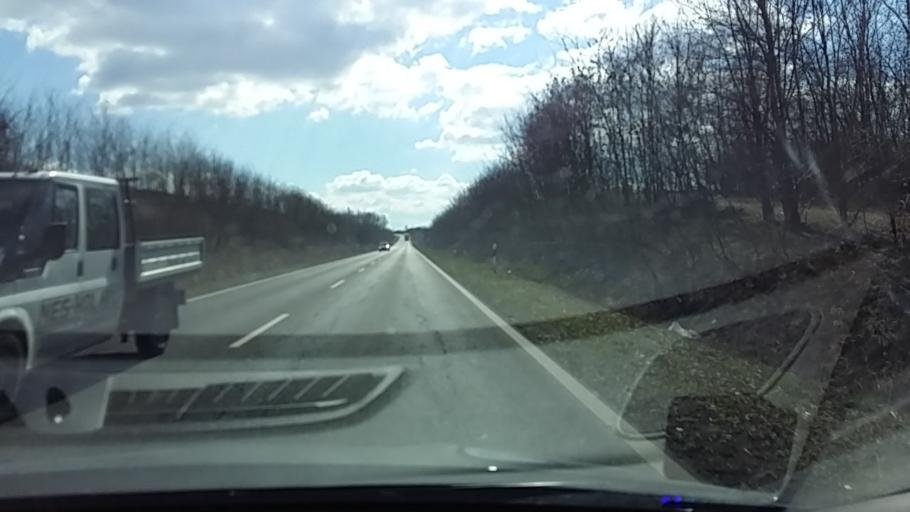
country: HU
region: Baranya
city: Kozarmisleny
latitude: 46.0500
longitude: 18.2743
